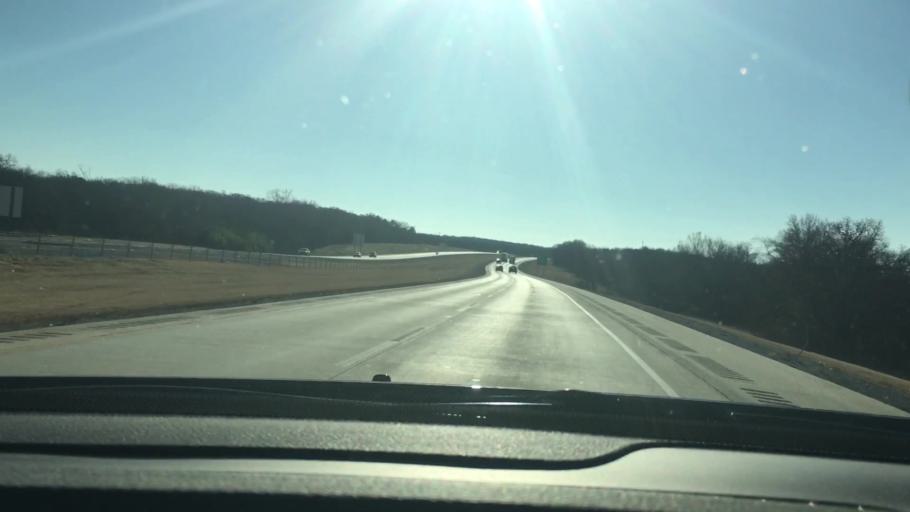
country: US
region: Oklahoma
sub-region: Carter County
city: Ardmore
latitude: 34.1576
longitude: -97.1630
